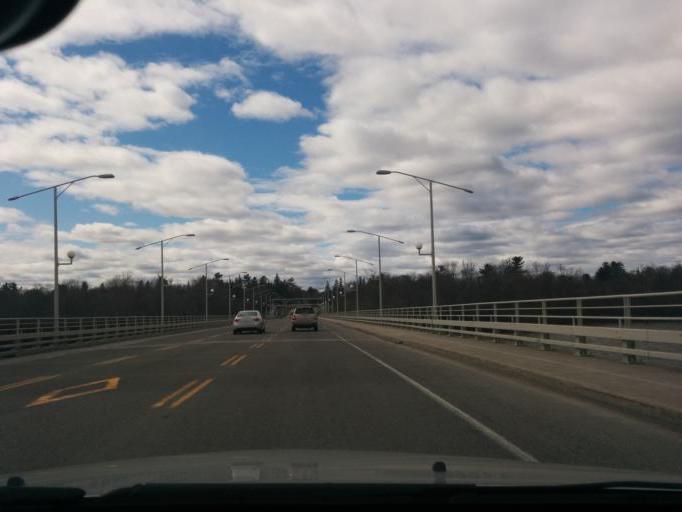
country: CA
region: Ontario
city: Ottawa
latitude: 45.4108
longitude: -75.7614
